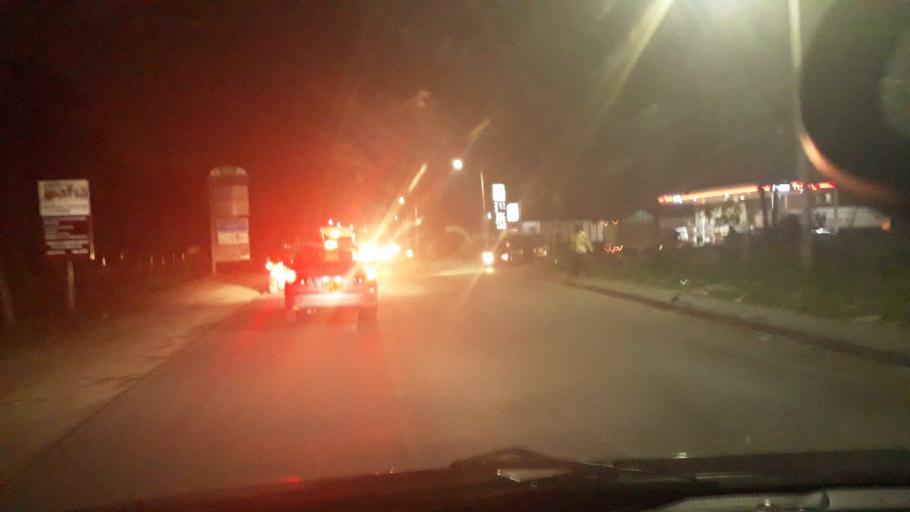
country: KE
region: Nairobi Area
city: Pumwani
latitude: -1.2658
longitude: 36.9042
